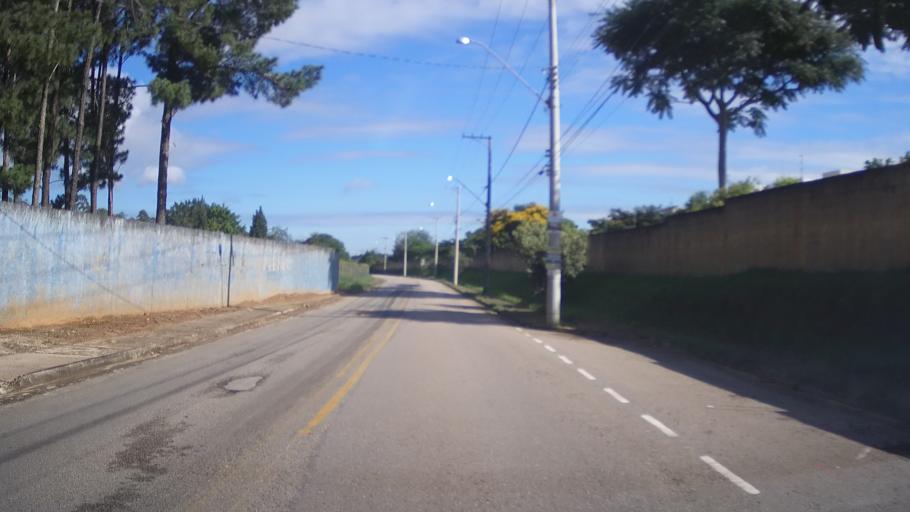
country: BR
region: Sao Paulo
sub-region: Itupeva
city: Itupeva
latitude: -23.2065
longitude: -47.0185
